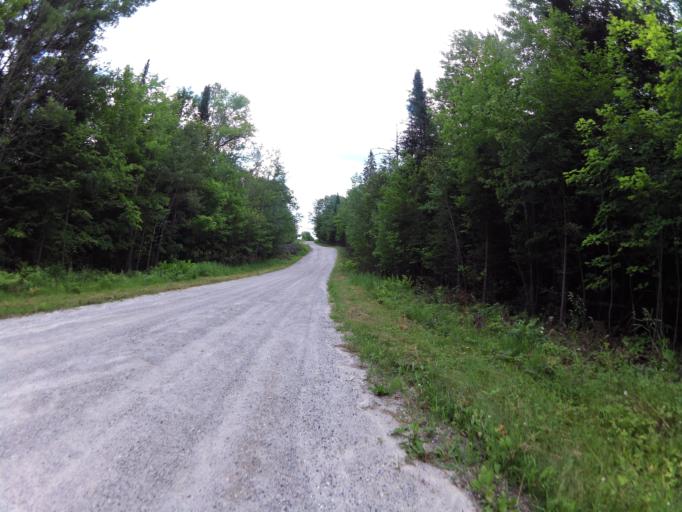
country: CA
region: Ontario
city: Perth
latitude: 45.0536
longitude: -76.4819
